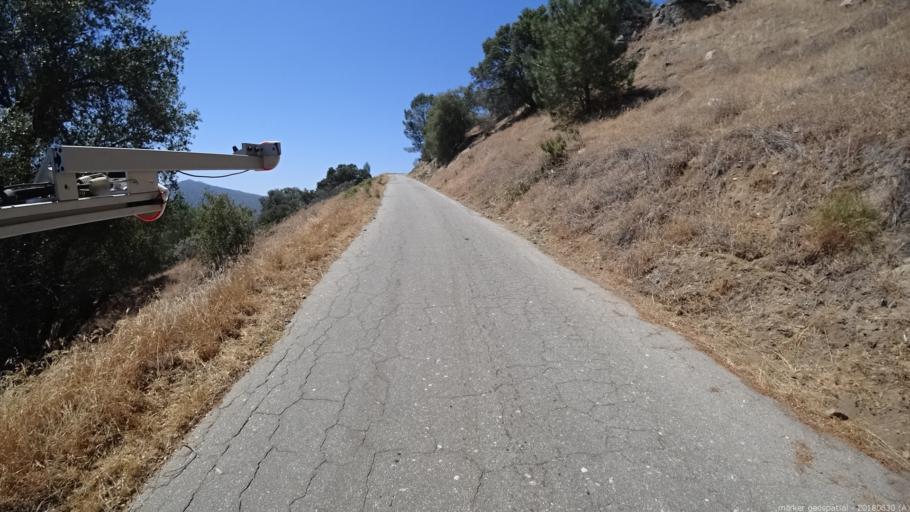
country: US
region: California
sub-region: Fresno County
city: Auberry
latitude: 37.1468
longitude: -119.4899
